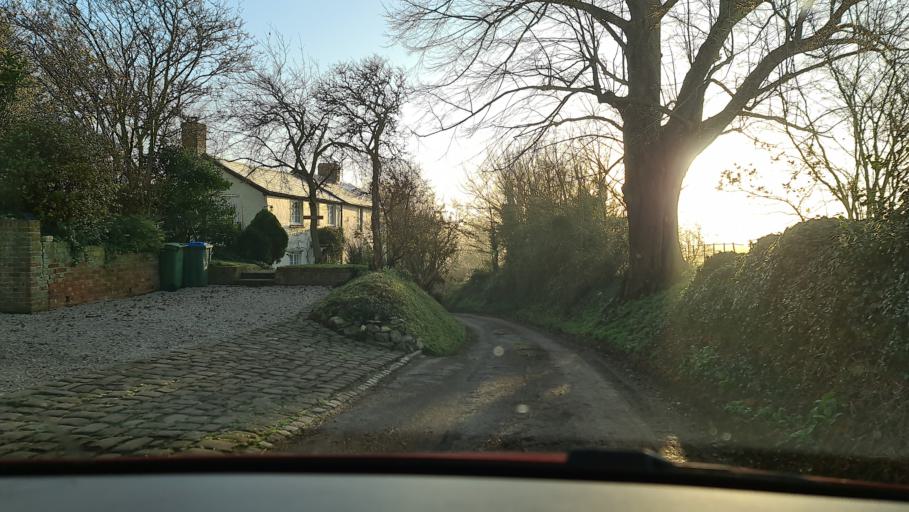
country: GB
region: England
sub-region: Buckinghamshire
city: Haddenham
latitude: 51.8066
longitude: -0.9429
